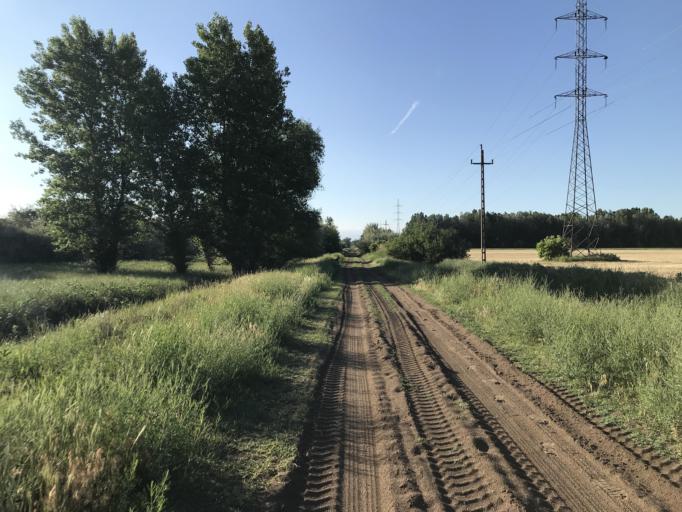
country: HU
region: Bacs-Kiskun
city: Tiszakecske
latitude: 46.9737
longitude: 20.0607
